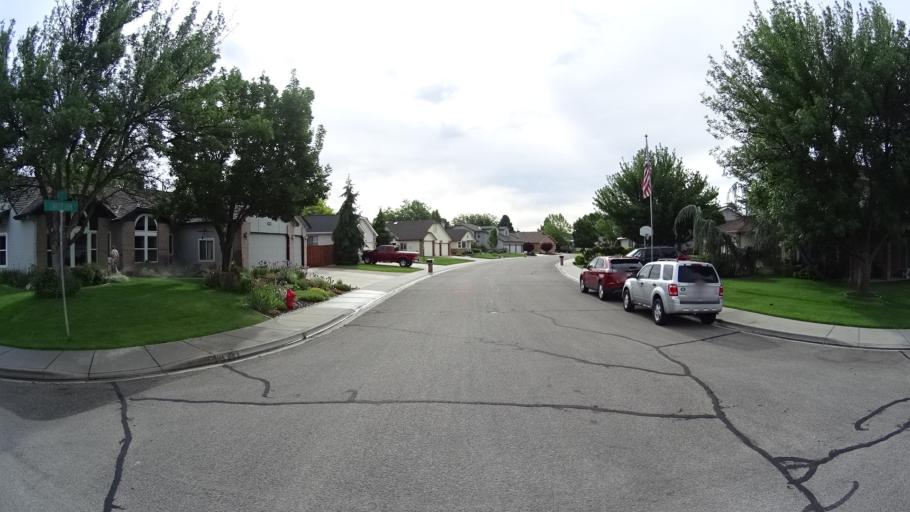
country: US
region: Idaho
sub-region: Ada County
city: Meridian
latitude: 43.5881
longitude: -116.3887
